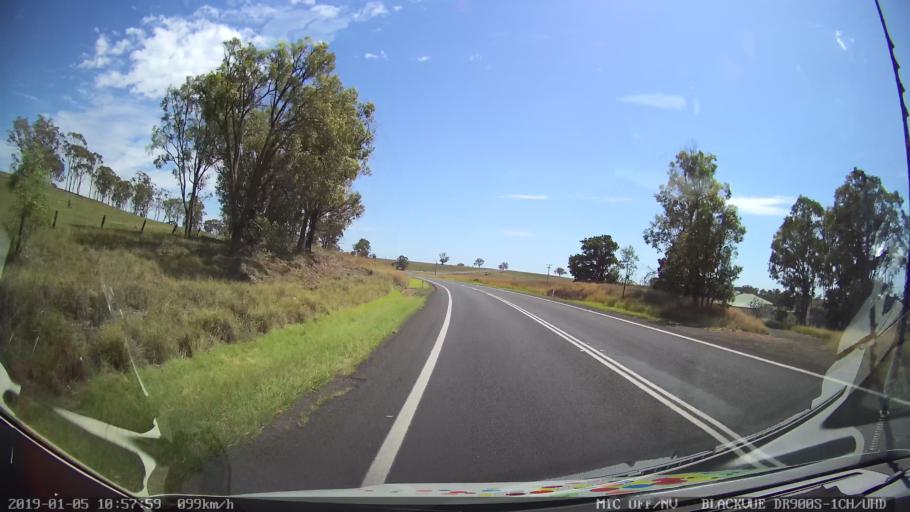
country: AU
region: New South Wales
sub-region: Warrumbungle Shire
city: Coonabarabran
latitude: -31.4263
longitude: 149.1765
